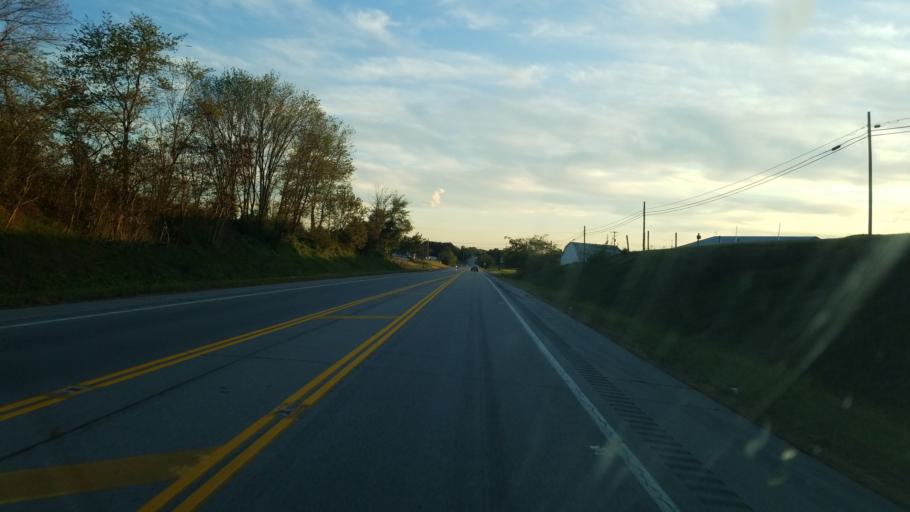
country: US
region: West Virginia
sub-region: Wood County
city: Washington
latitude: 39.2013
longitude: -81.8285
